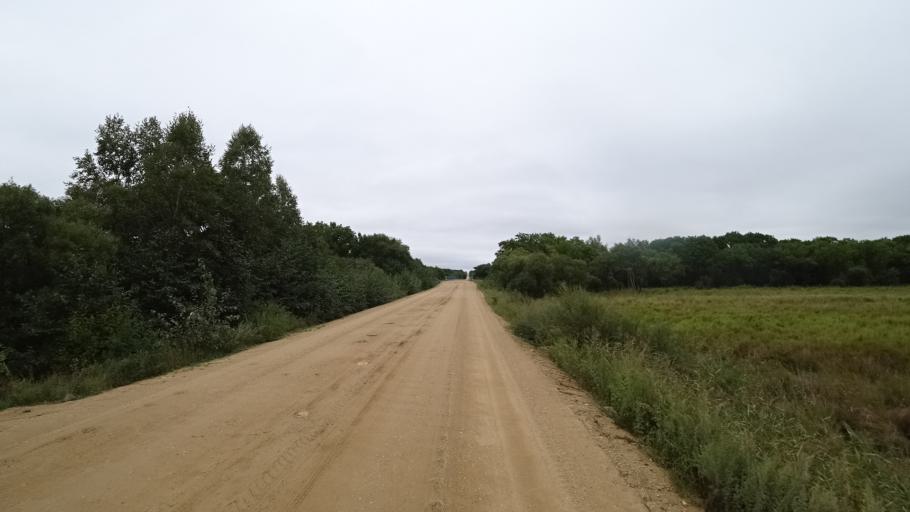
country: RU
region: Primorskiy
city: Ivanovka
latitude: 44.0656
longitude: 132.5732
